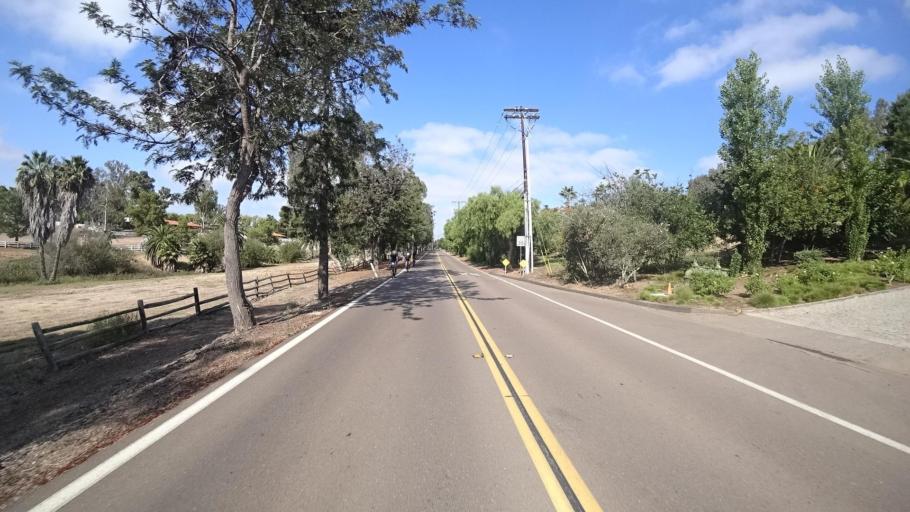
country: US
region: California
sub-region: San Diego County
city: Rancho Santa Fe
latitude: 33.0439
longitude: -117.2032
